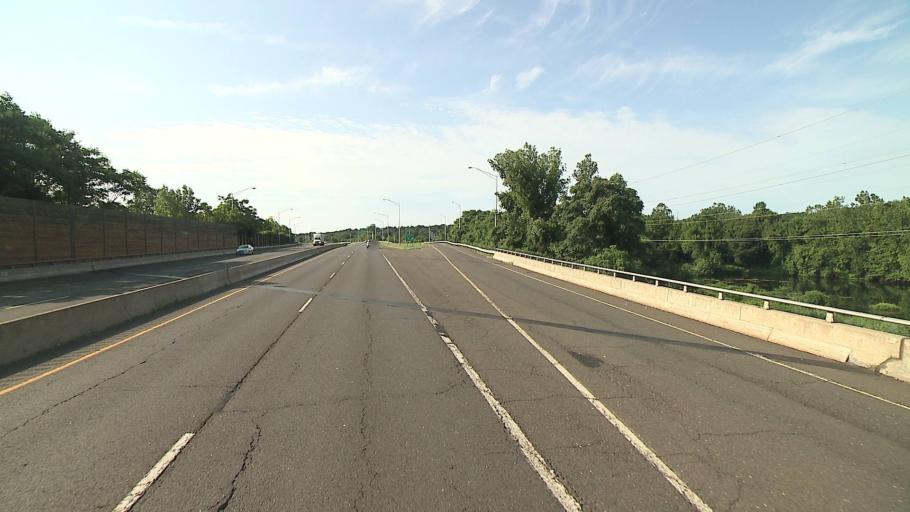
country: US
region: Connecticut
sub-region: Fairfield County
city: Norwalk
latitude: 41.1318
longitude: -73.4287
